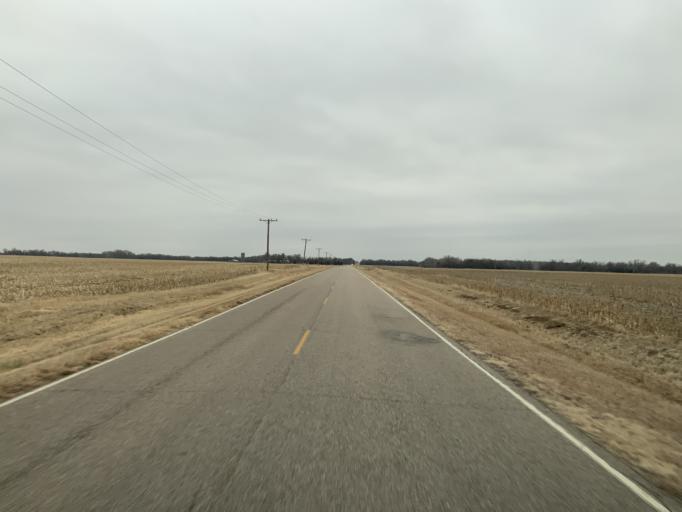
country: US
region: Kansas
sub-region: Reno County
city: South Hutchinson
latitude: 37.9502
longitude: -98.0874
